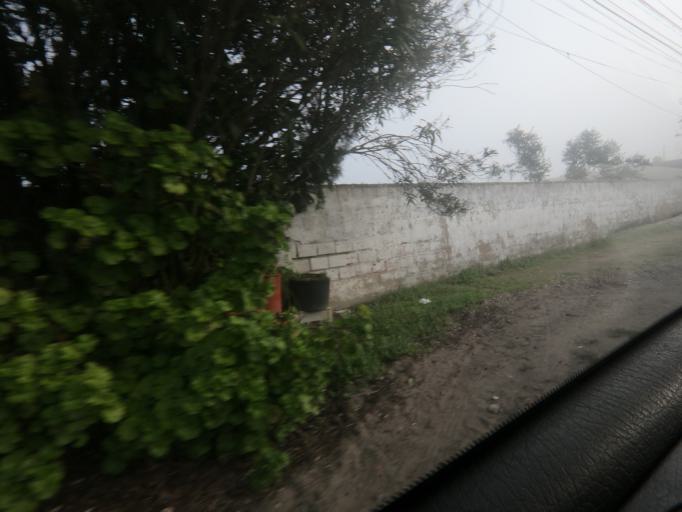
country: PT
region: Setubal
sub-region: Palmela
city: Pinhal Novo
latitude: 38.6124
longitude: -8.8779
